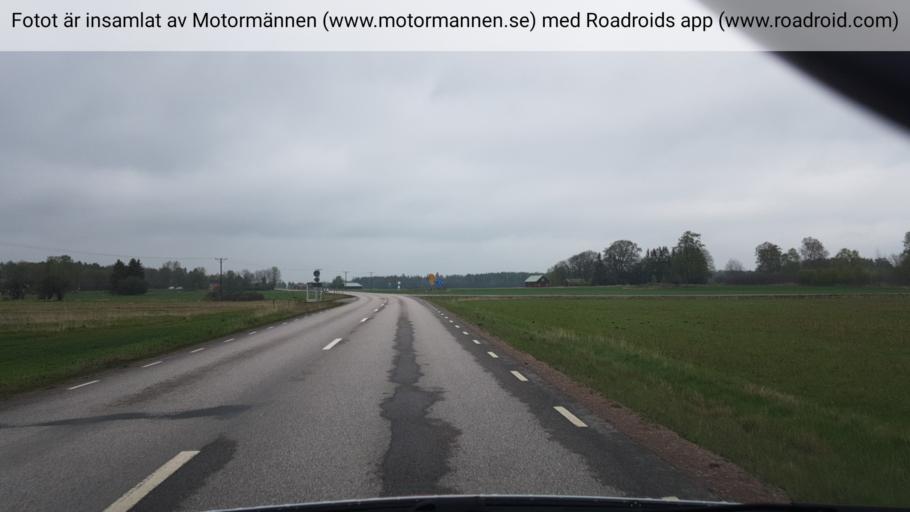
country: SE
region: Vaestra Goetaland
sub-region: Skovde Kommun
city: Stopen
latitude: 58.5356
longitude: 13.9971
